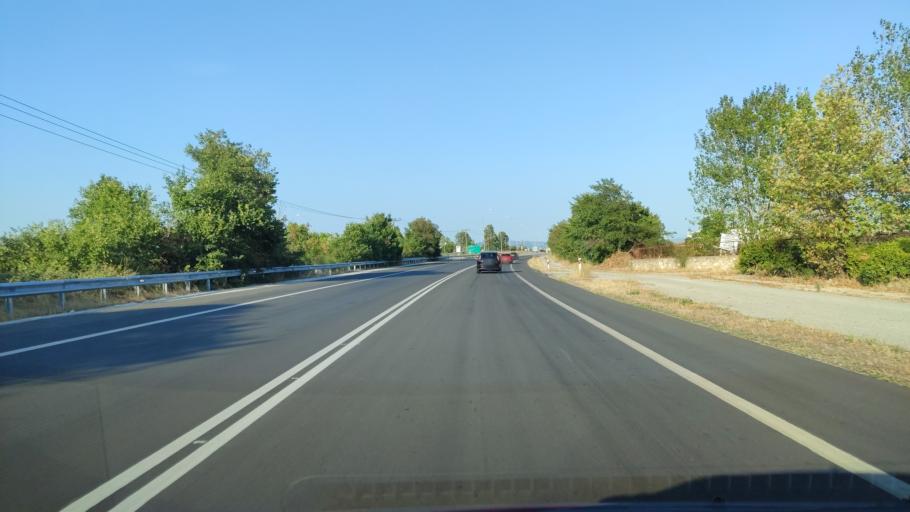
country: GR
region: East Macedonia and Thrace
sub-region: Nomos Rodopis
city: Komotini
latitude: 41.1030
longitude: 25.3265
